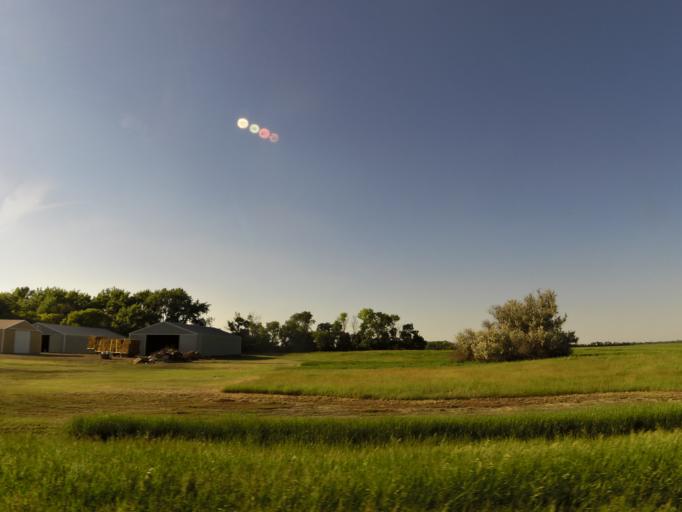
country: US
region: North Dakota
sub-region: Grand Forks County
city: Grand Forks Air Force Base
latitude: 48.1356
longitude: -97.2008
